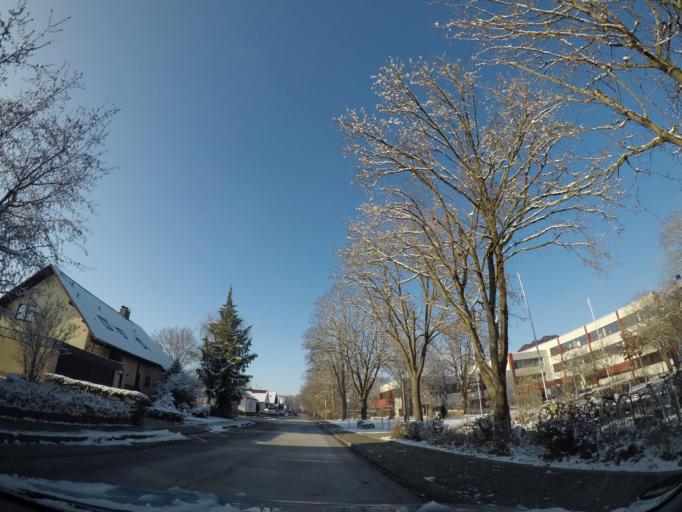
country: DE
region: Bavaria
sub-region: Swabia
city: Senden
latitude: 48.3021
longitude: 10.0542
